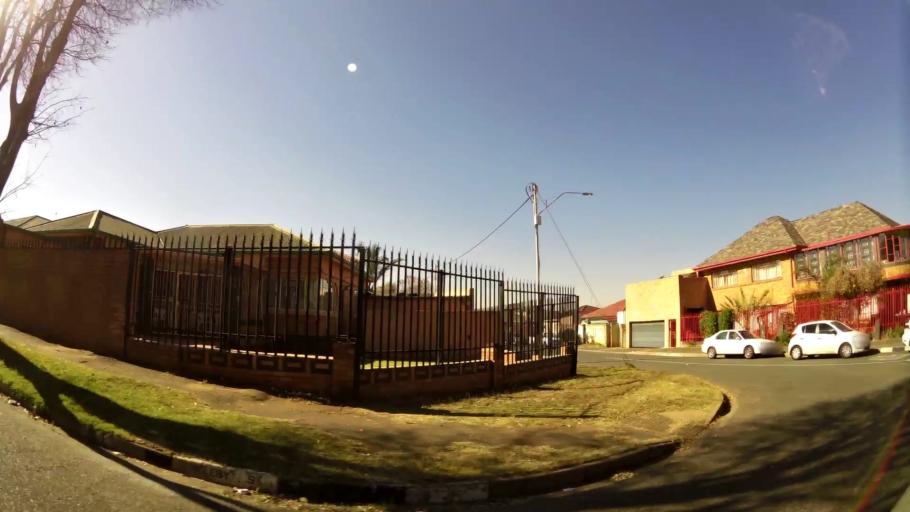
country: ZA
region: Gauteng
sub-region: City of Johannesburg Metropolitan Municipality
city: Johannesburg
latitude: -26.1920
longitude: 27.9907
